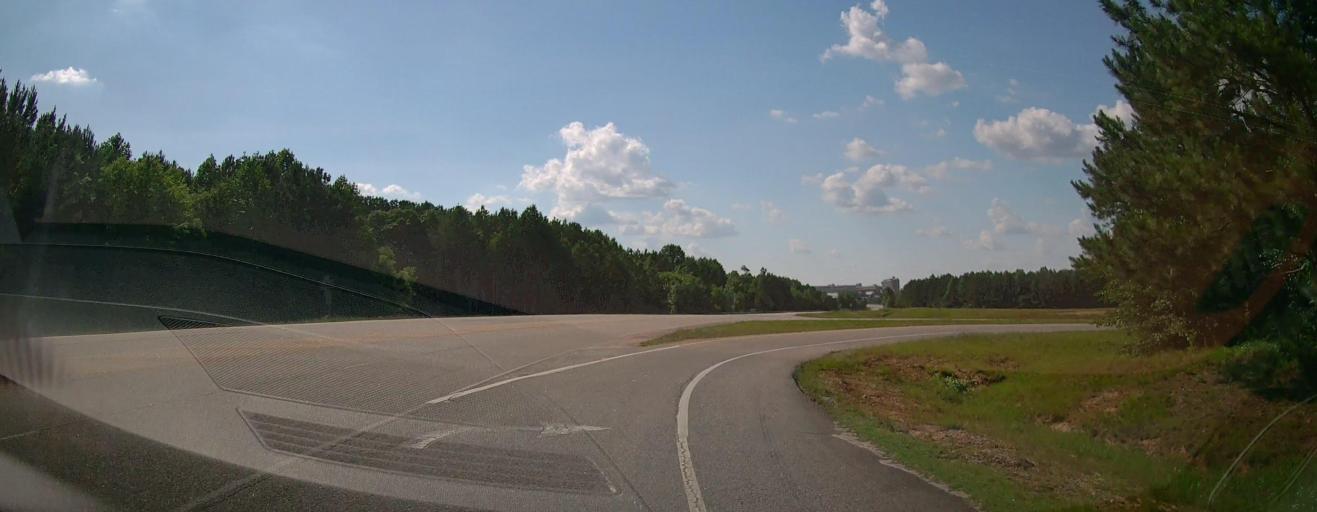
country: US
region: Georgia
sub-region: Henry County
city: Hampton
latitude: 33.3703
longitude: -84.3038
